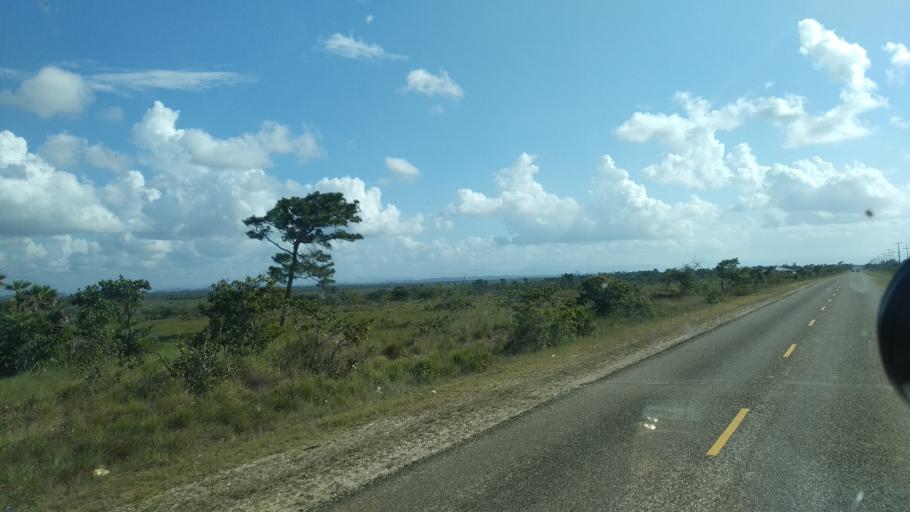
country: BZ
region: Cayo
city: Belmopan
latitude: 17.4005
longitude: -88.5058
